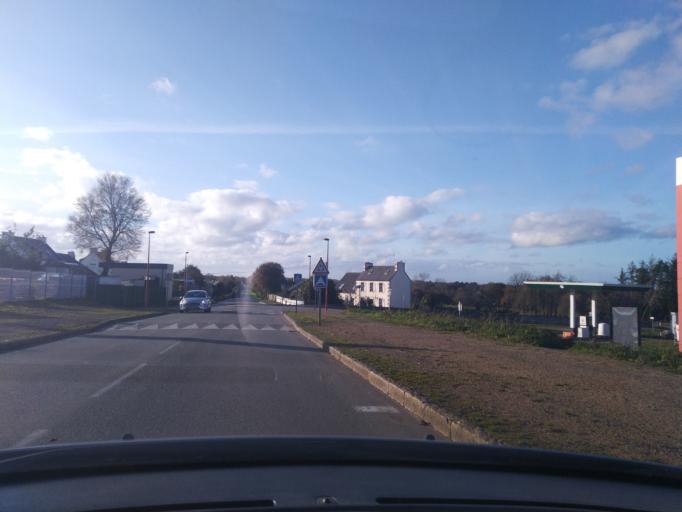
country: FR
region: Brittany
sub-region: Departement du Finistere
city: Plouigneau
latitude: 48.5699
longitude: -3.7071
